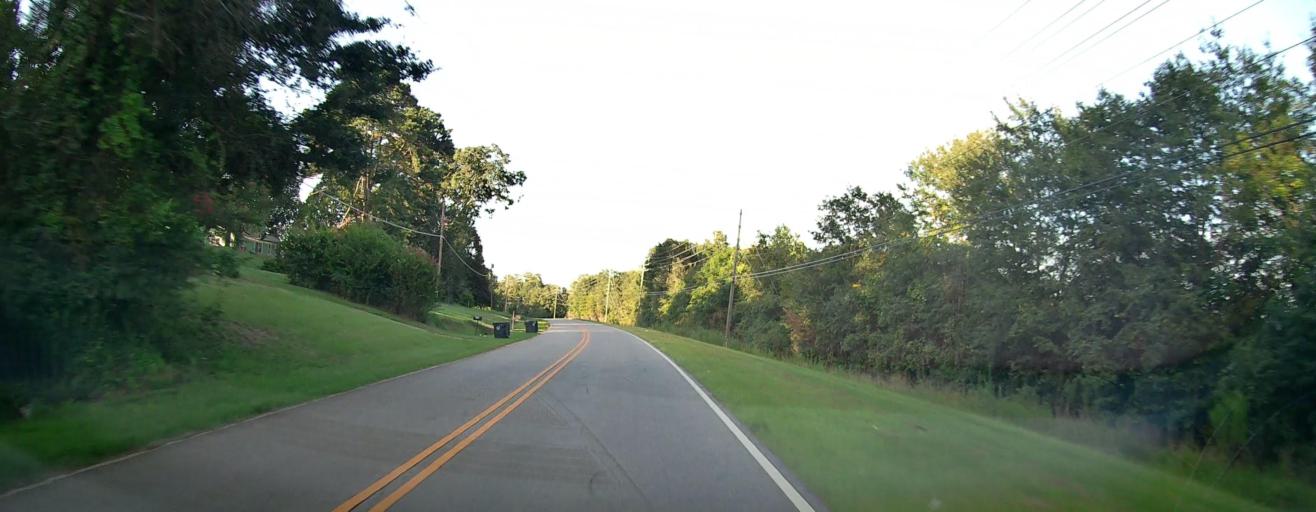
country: US
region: Georgia
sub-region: Muscogee County
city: Columbus
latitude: 32.4263
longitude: -85.0159
